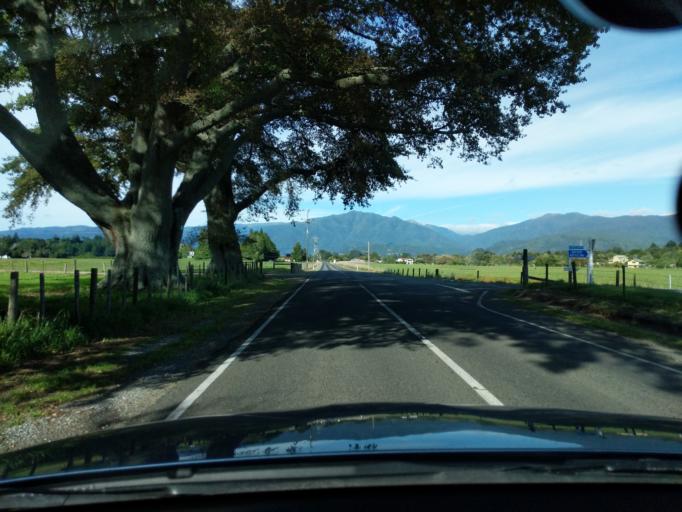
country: NZ
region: Tasman
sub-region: Tasman District
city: Takaka
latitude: -40.8515
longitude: 172.8301
